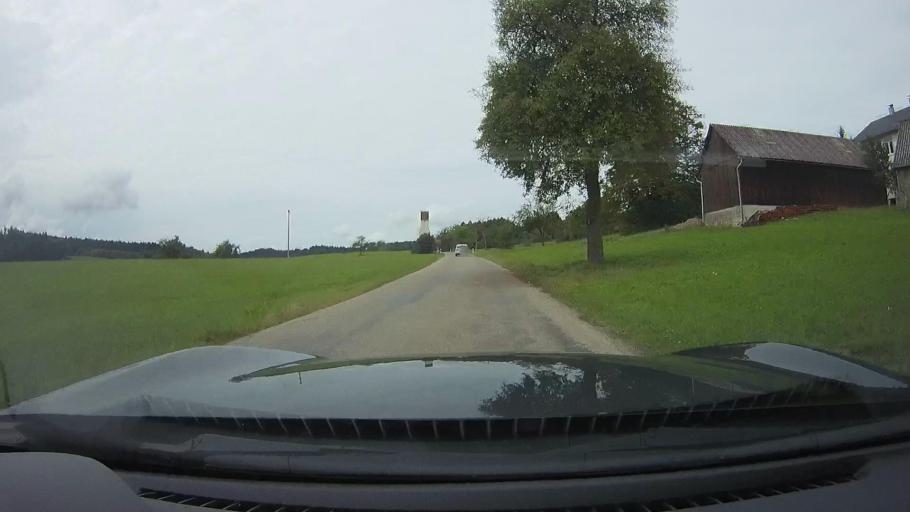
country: DE
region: Baden-Wuerttemberg
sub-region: Regierungsbezirk Stuttgart
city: Murrhardt
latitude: 49.0252
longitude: 9.5684
